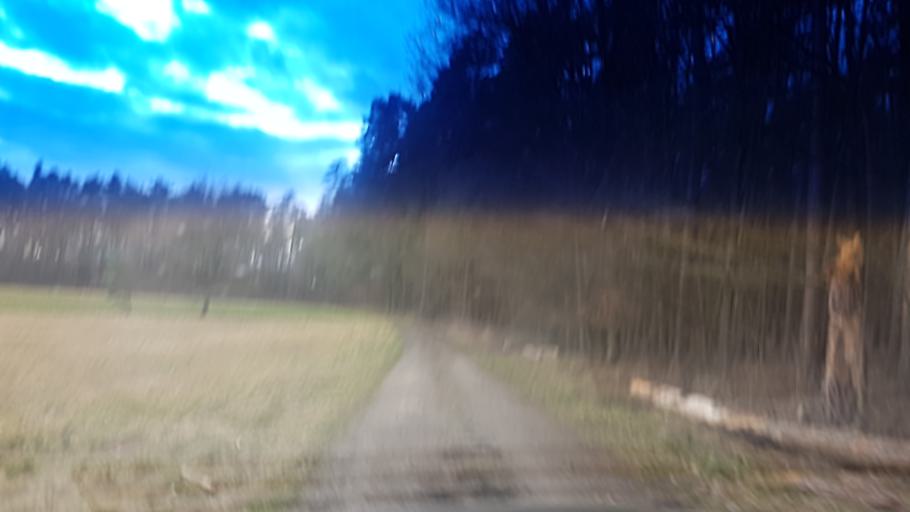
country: DE
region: Bavaria
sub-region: Upper Franconia
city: Lauter
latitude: 49.9571
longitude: 10.7695
